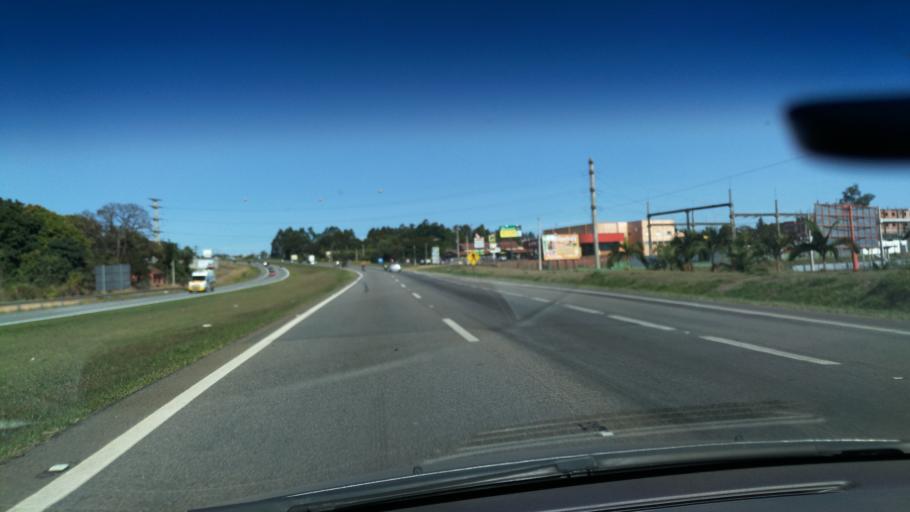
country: BR
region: Sao Paulo
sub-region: Jaguariuna
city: Jaguariuna
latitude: -22.6232
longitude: -47.0071
